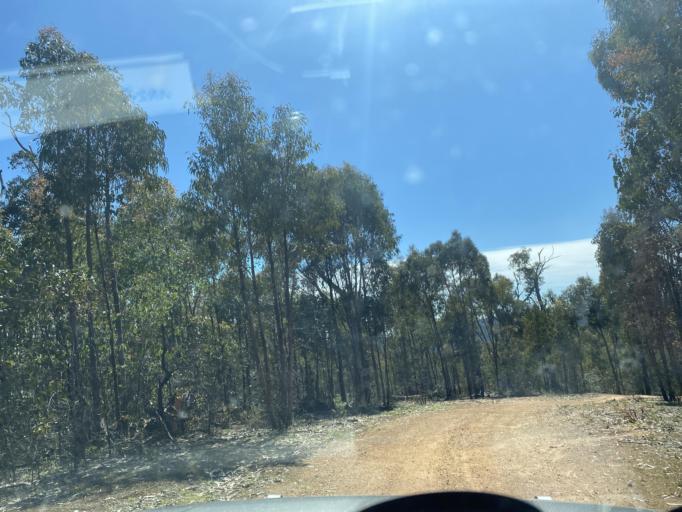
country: AU
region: Victoria
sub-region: Benalla
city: Benalla
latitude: -36.7383
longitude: 146.1799
